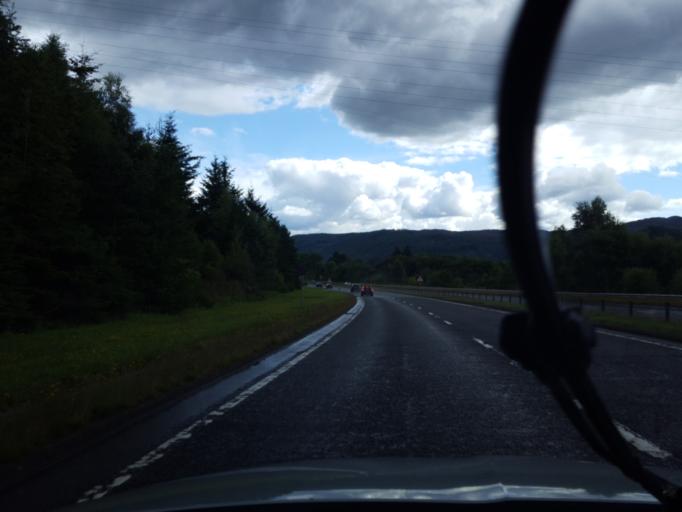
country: GB
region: Scotland
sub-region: Perth and Kinross
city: Pitlochry
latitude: 56.7271
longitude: -3.7735
